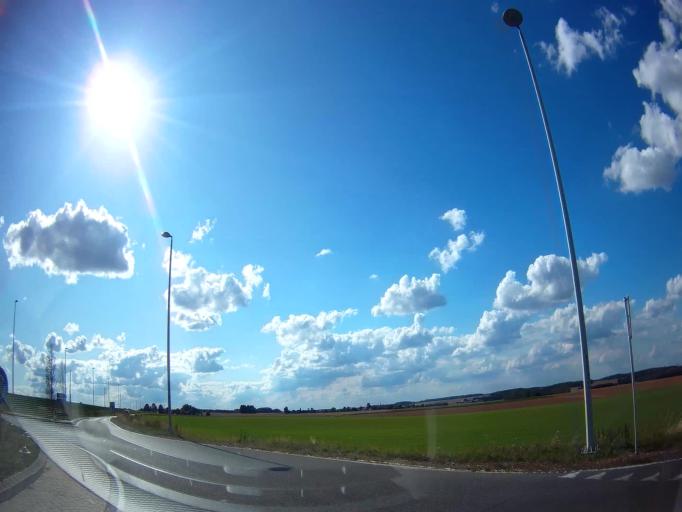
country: BE
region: Wallonia
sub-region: Province de Namur
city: Mettet
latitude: 50.3222
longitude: 4.7405
